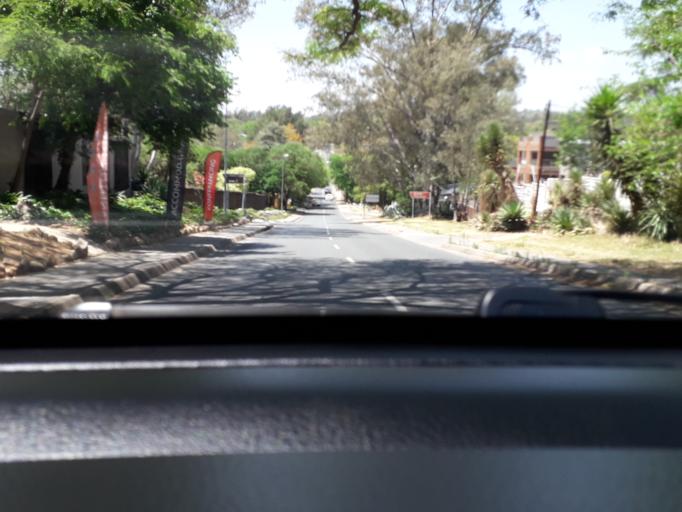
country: ZA
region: Gauteng
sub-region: City of Johannesburg Metropolitan Municipality
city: Midrand
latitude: -26.0483
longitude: 28.0648
